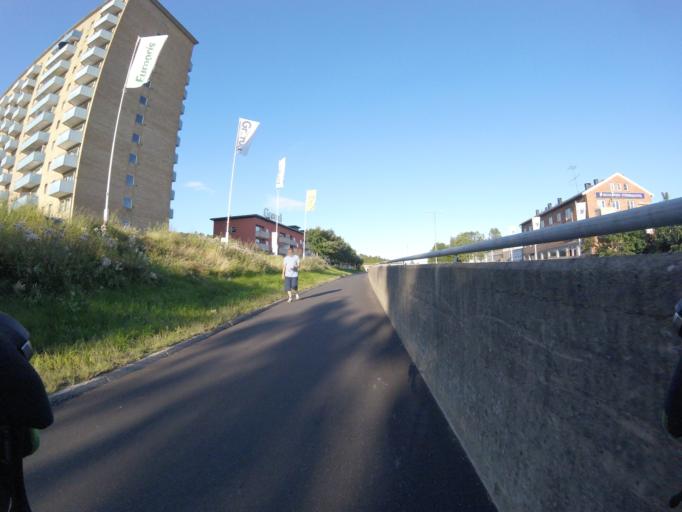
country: NO
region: Akershus
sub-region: Lorenskog
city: Kjenn
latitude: 59.9597
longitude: 10.8805
